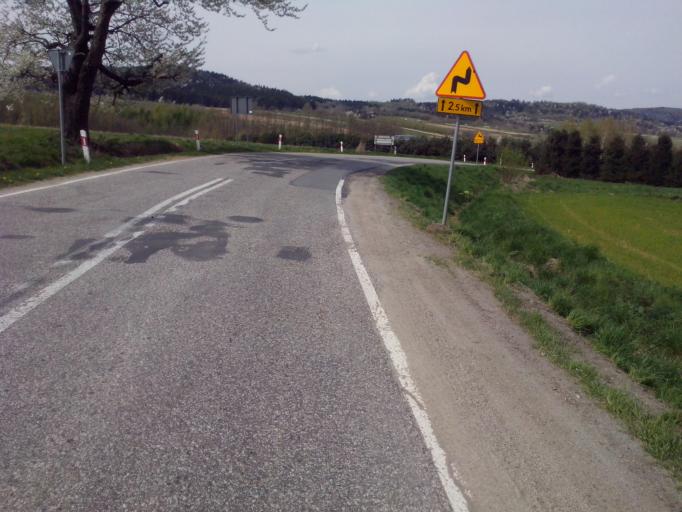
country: PL
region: Subcarpathian Voivodeship
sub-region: Powiat strzyzowski
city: Jawornik
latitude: 49.8025
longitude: 21.8650
